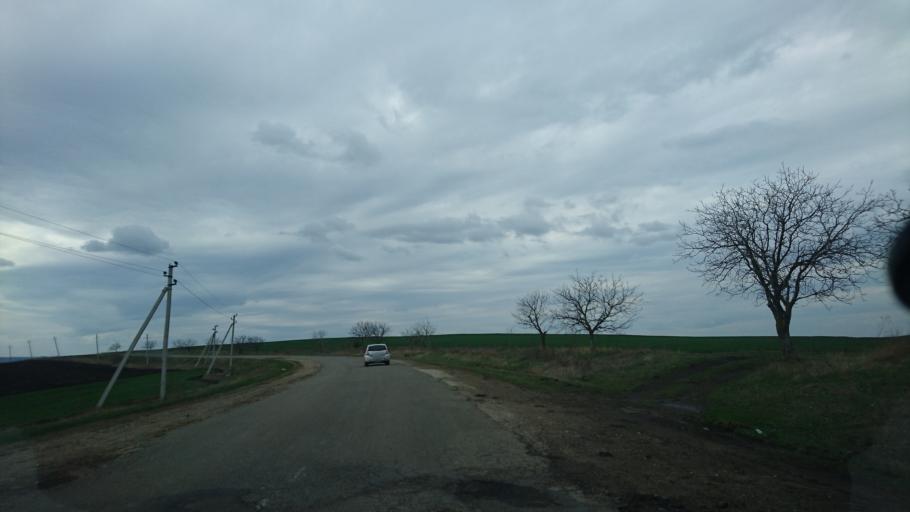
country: MD
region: Cantemir
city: Visniovca
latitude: 46.3207
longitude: 28.5451
